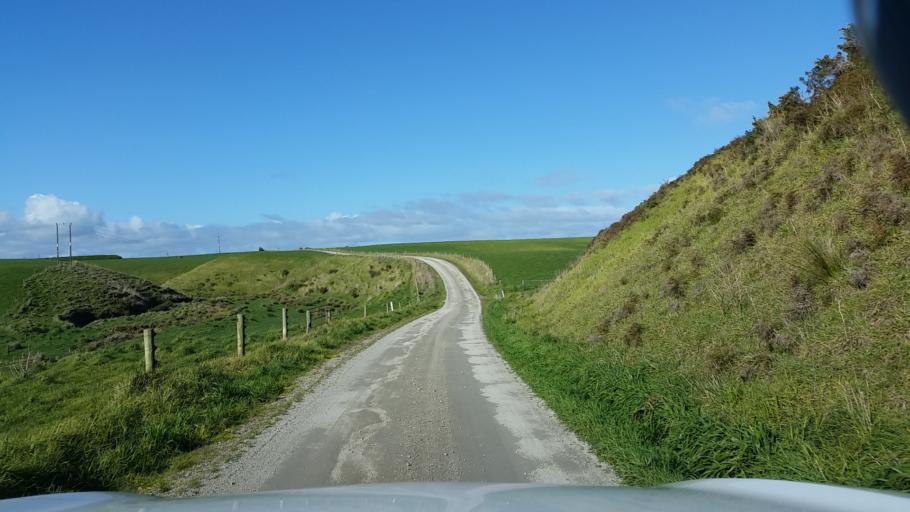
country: NZ
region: Taranaki
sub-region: South Taranaki District
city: Patea
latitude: -39.6835
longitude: 174.3913
